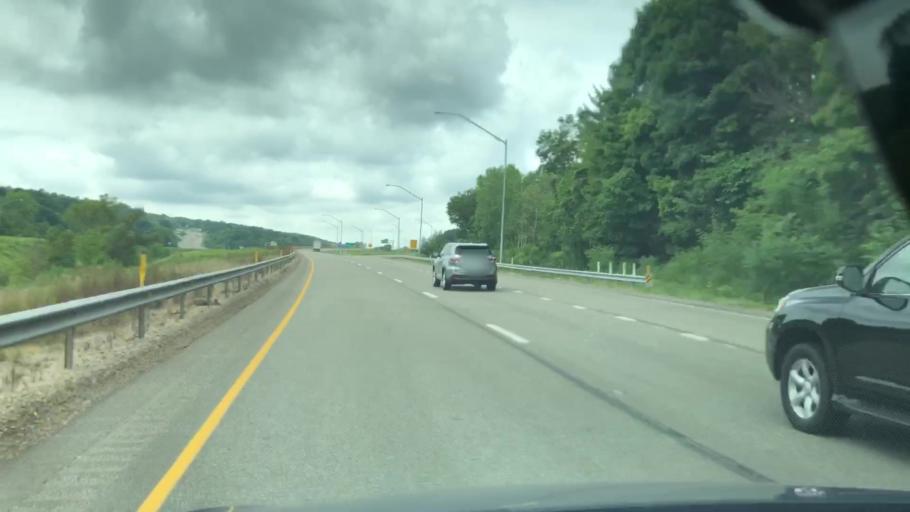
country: US
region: Pennsylvania
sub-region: Crawford County
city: Meadville
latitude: 41.6187
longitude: -80.1745
